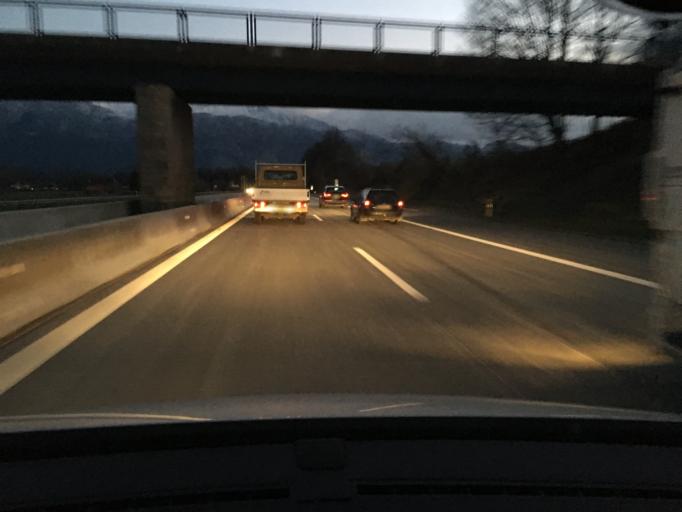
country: DE
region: Bavaria
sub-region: Upper Bavaria
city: Oberaudorf
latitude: 47.6519
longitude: 12.1868
